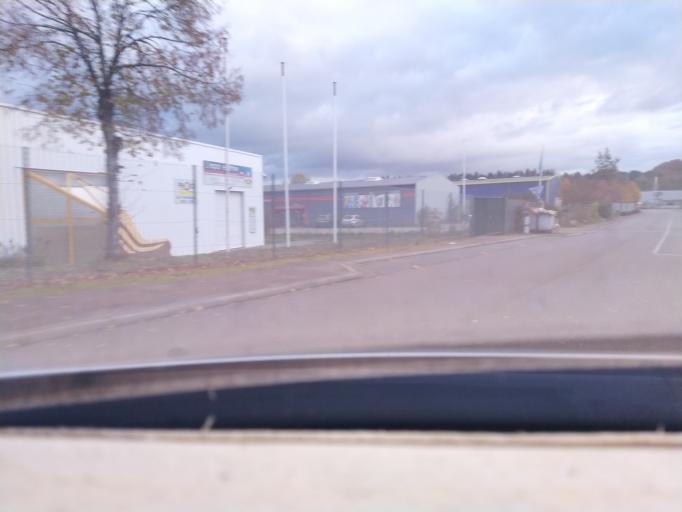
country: FR
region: Haute-Normandie
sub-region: Departement de la Seine-Maritime
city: Yainville
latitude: 49.4584
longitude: 0.8224
